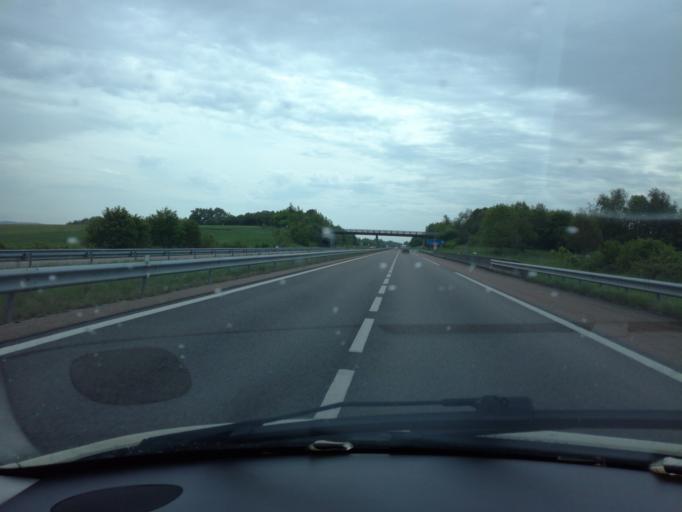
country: FR
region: Franche-Comte
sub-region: Departement du Jura
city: Mont-sous-Vaudrey
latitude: 46.8756
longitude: 5.5832
